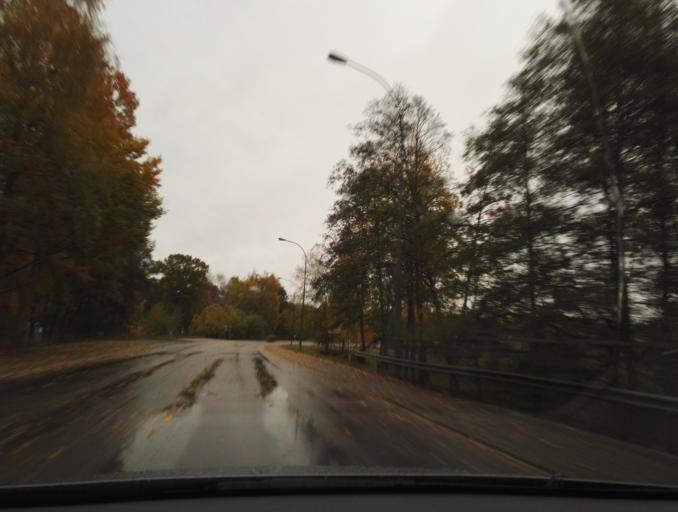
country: SE
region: Kronoberg
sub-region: Vaxjo Kommun
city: Vaexjoe
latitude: 56.8924
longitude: 14.7406
